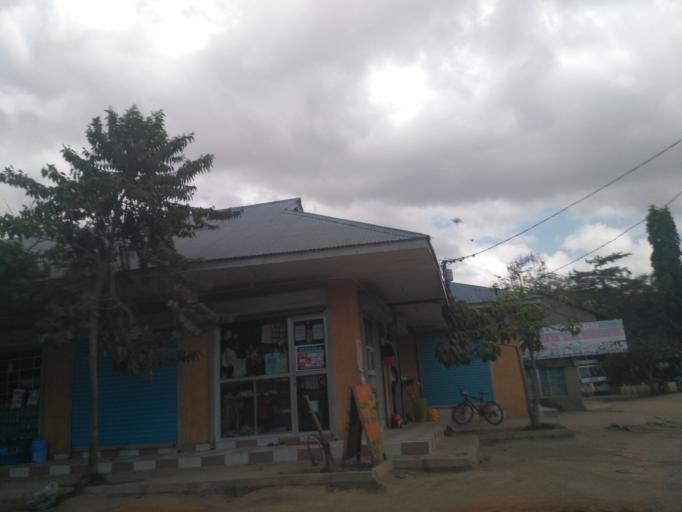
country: TZ
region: Dar es Salaam
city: Dar es Salaam
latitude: -6.8924
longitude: 39.2840
